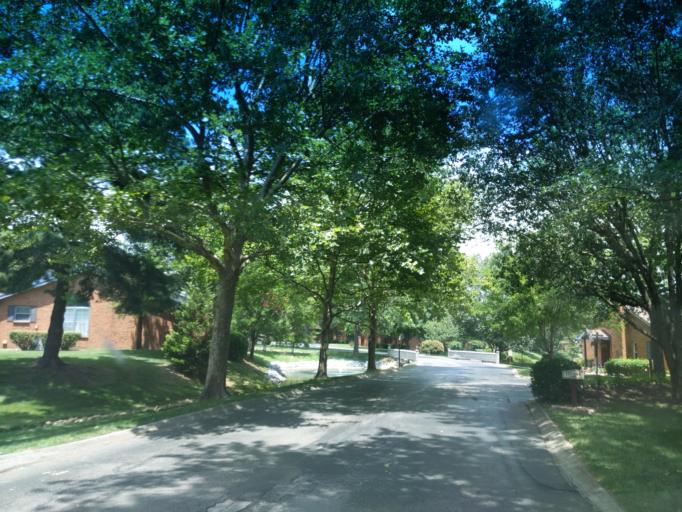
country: US
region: Tennessee
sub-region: Williamson County
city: Brentwood
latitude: 36.0410
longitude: -86.7652
